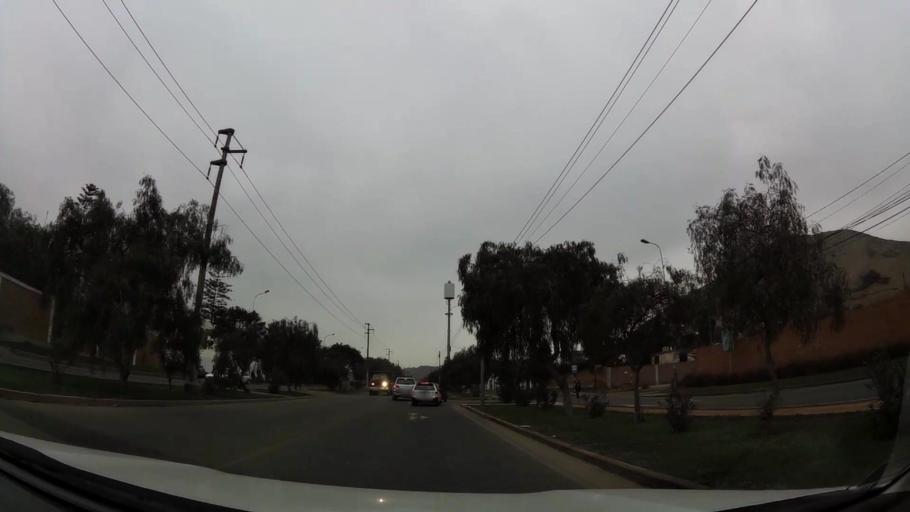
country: PE
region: Lima
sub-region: Lima
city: La Molina
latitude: -12.0861
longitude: -76.8968
